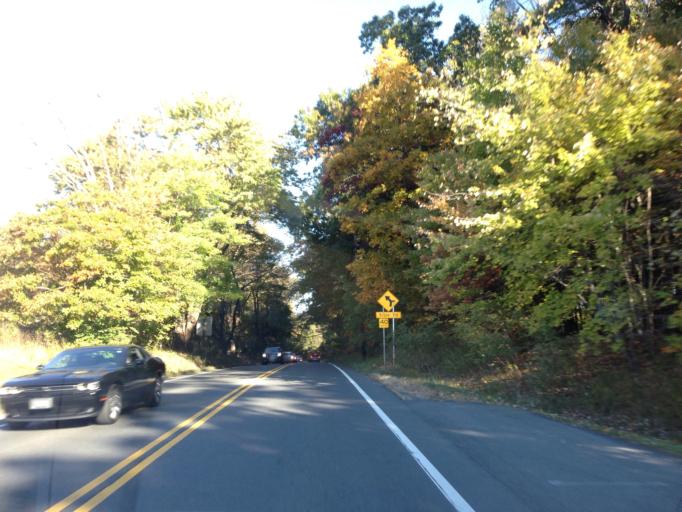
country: US
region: Maryland
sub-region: Montgomery County
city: Clarksburg
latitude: 39.2120
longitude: -77.2484
